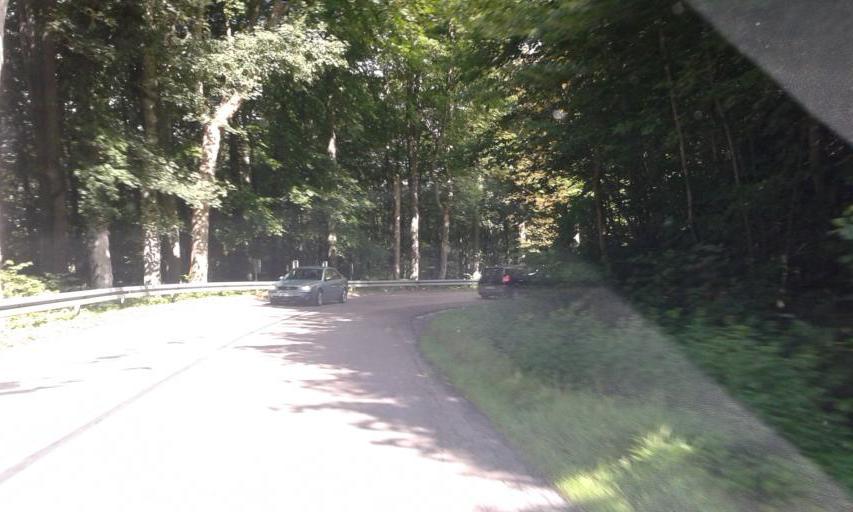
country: PL
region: West Pomeranian Voivodeship
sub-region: Powiat koszalinski
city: Polanow
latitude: 53.9995
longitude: 16.7157
